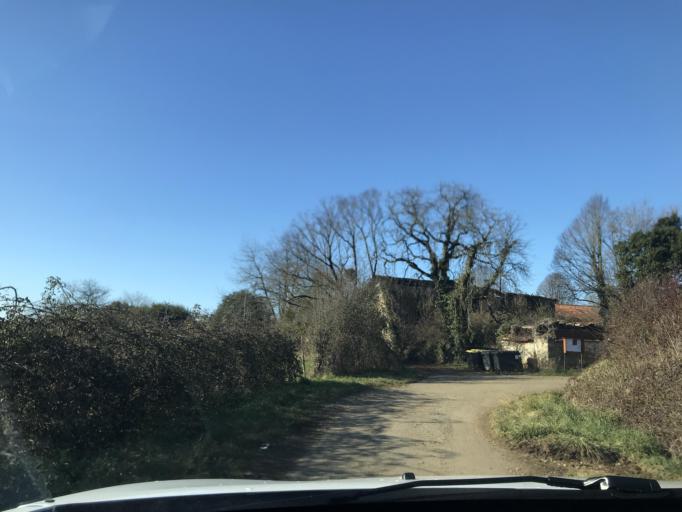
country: FR
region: Poitou-Charentes
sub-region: Departement de la Charente
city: Chasseneuil-sur-Bonnieure
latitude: 45.8436
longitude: 0.5181
